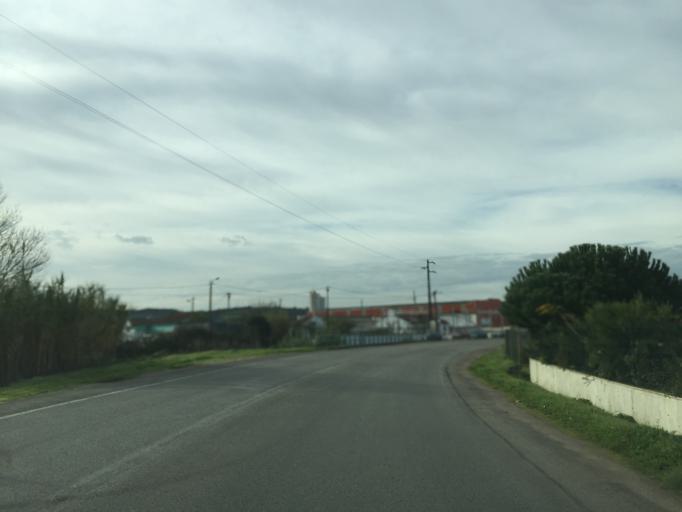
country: PT
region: Lisbon
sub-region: Sintra
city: Pero Pinheiro
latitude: 38.8648
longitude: -9.2994
